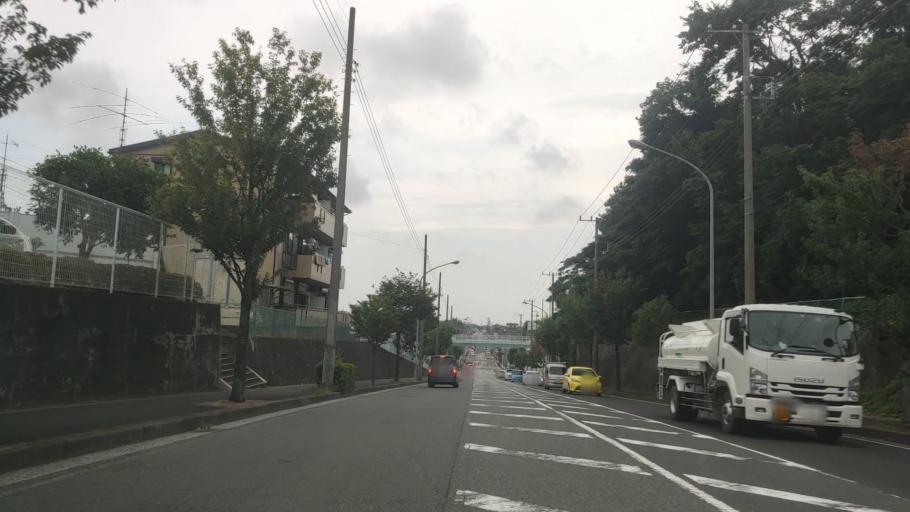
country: JP
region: Kanagawa
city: Minami-rinkan
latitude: 35.4555
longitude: 139.4818
